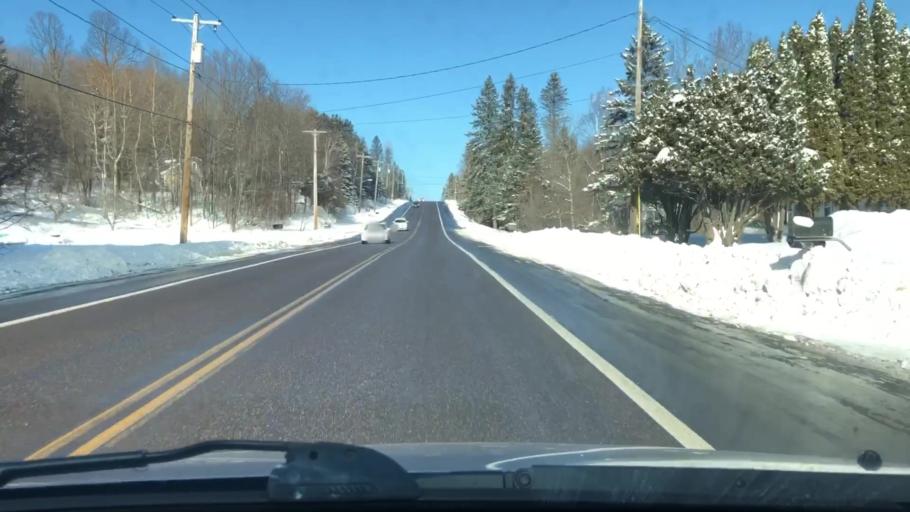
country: US
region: Minnesota
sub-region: Saint Louis County
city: Duluth
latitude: 46.8100
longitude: -92.1321
